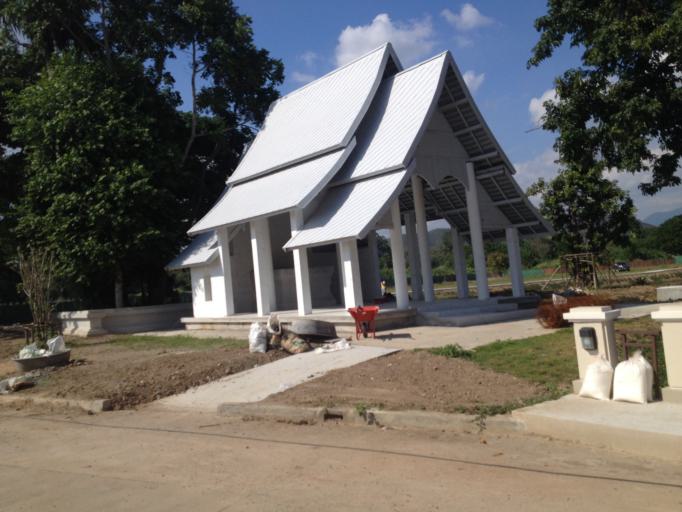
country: TH
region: Chiang Mai
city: Hang Dong
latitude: 18.7100
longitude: 98.9086
